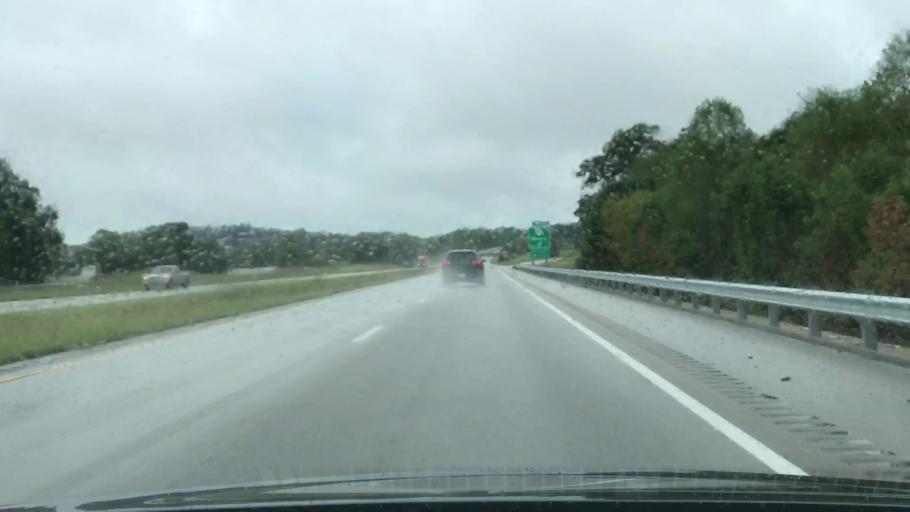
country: US
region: Kentucky
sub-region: Pulaski County
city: Somerset
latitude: 37.0945
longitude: -84.7942
